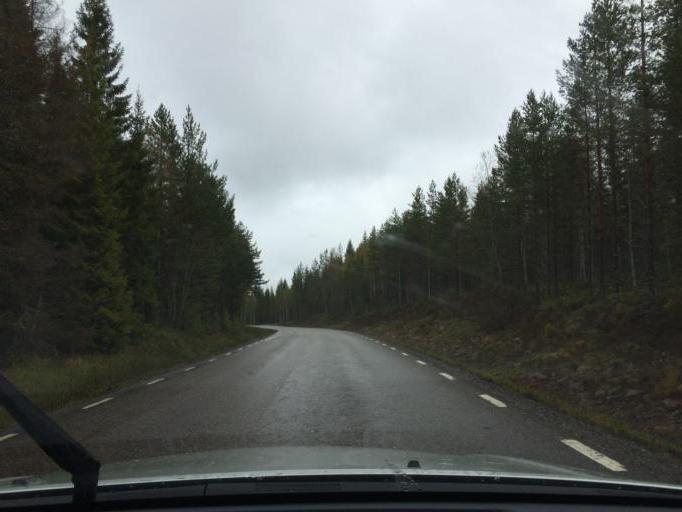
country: SE
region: Dalarna
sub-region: Ludvika Kommun
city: Abborrberget
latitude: 60.0633
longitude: 14.8423
